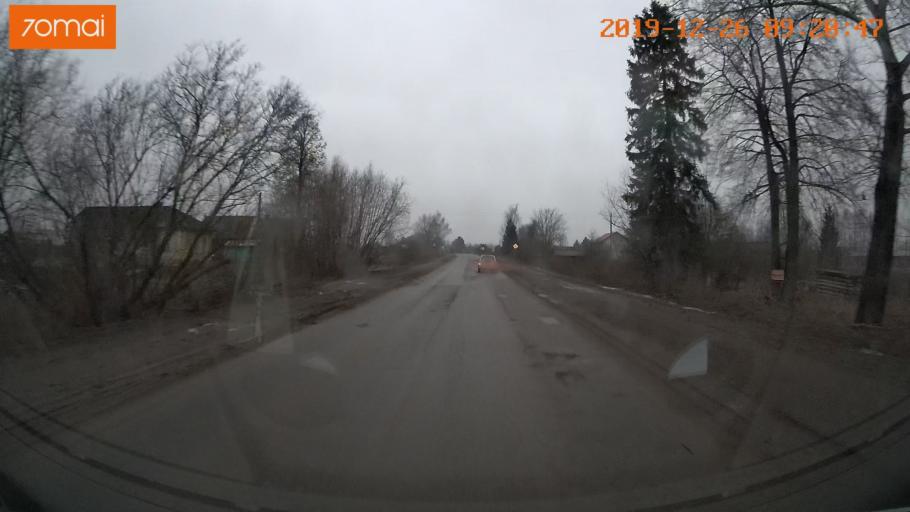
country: RU
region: Vologda
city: Gryazovets
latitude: 58.9643
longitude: 40.2277
